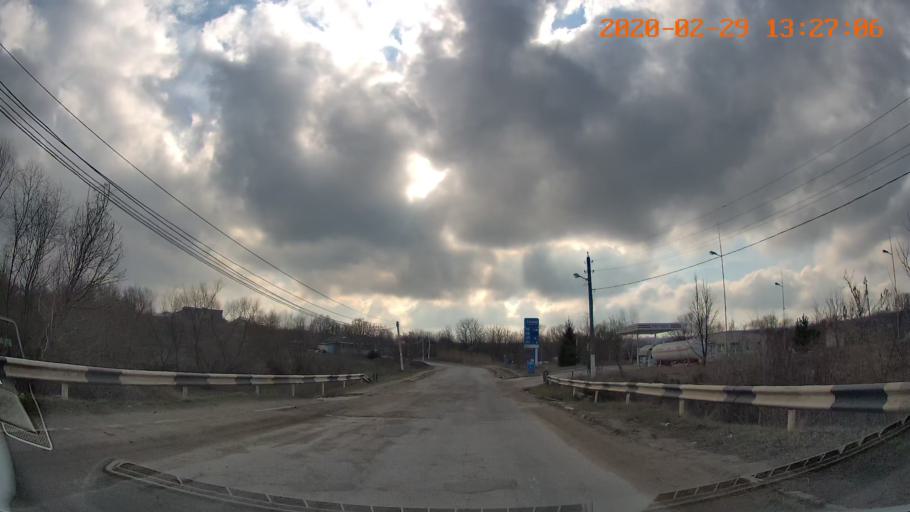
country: MD
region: Telenesti
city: Camenca
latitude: 47.9144
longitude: 28.6400
